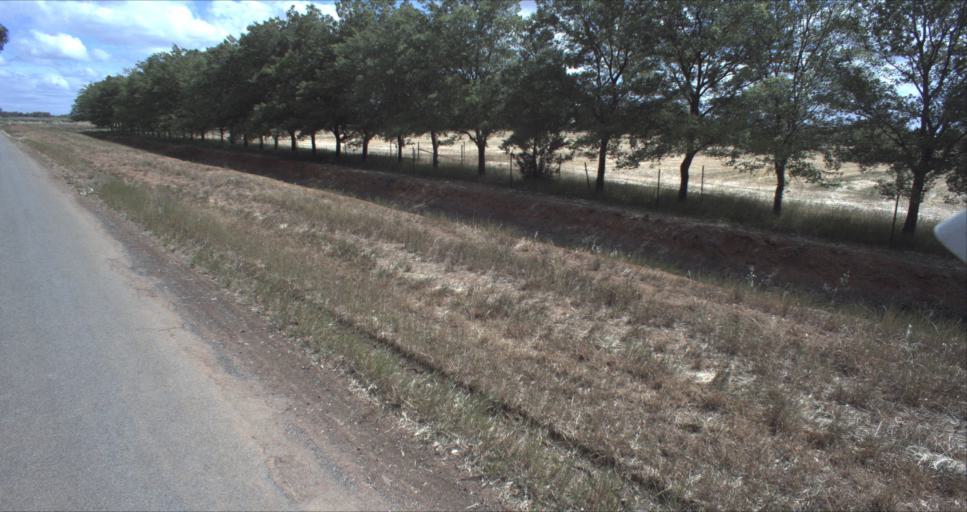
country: AU
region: New South Wales
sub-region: Leeton
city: Leeton
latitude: -34.5878
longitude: 146.3957
